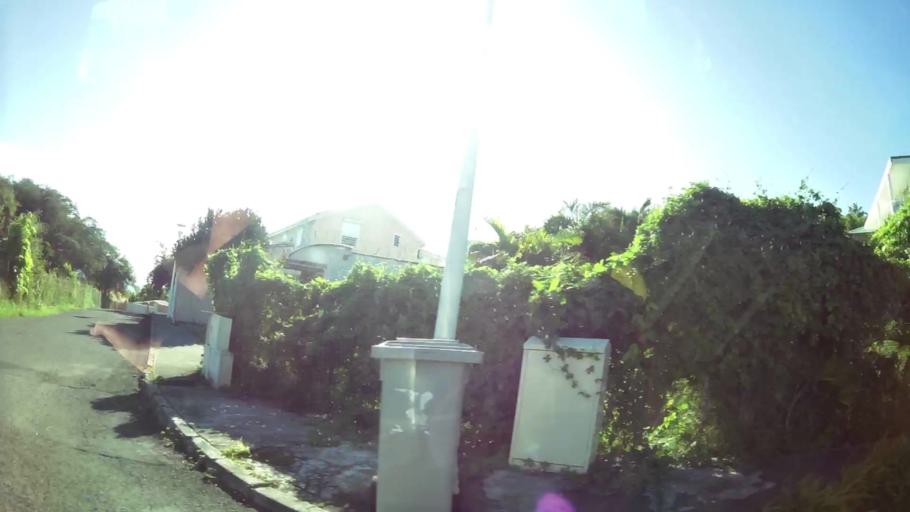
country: GP
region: Guadeloupe
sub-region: Guadeloupe
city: Le Gosier
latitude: 16.2026
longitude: -61.4747
